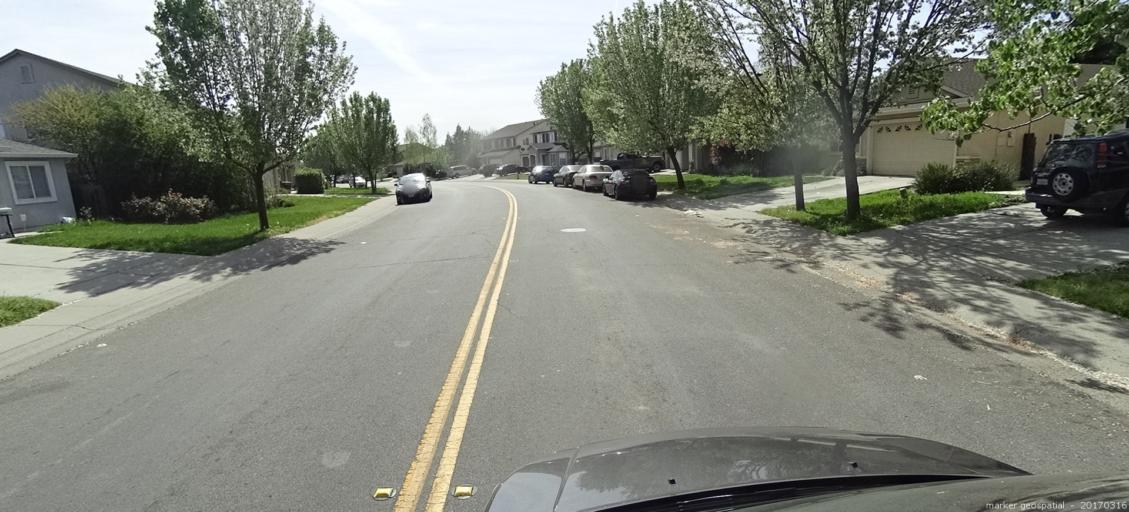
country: US
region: California
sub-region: Sacramento County
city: Parkway
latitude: 38.4758
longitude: -121.5007
